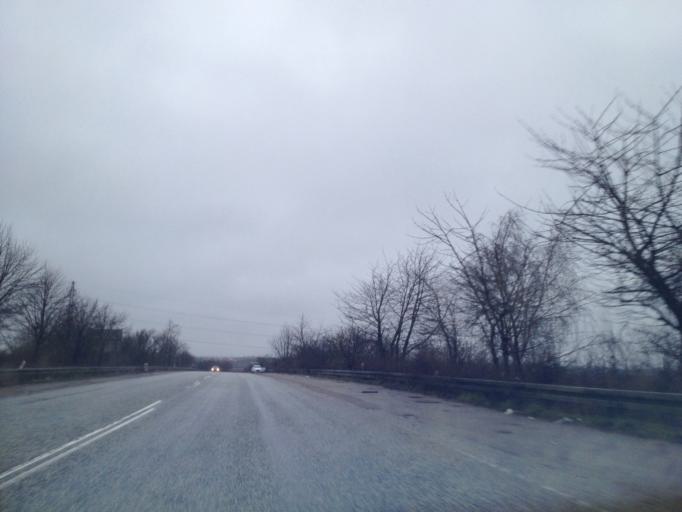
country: DK
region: Capital Region
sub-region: Hoje-Taastrup Kommune
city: Flong
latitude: 55.6477
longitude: 12.1606
